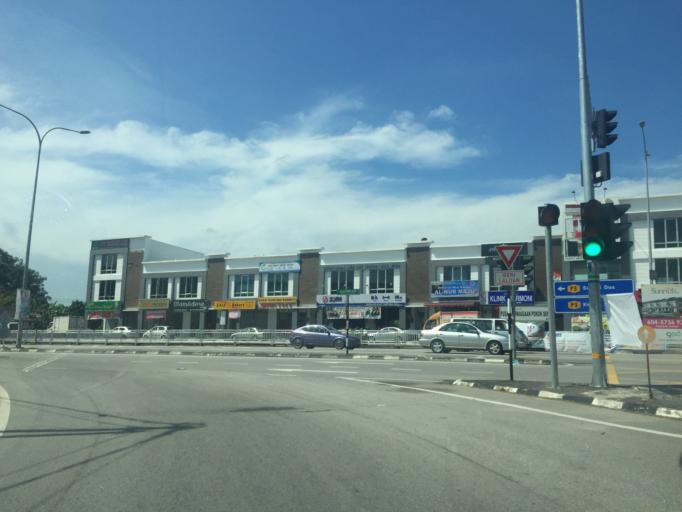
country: MY
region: Penang
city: Tasek Glugor
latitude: 5.4887
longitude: 100.4577
